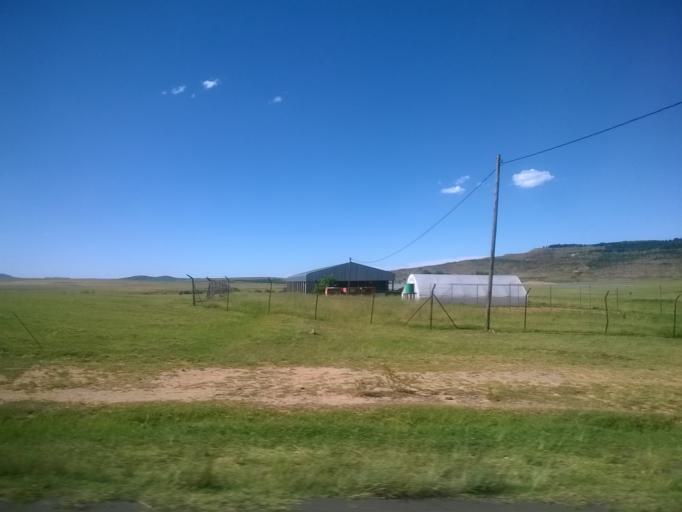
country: LS
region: Maseru
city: Maseru
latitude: -29.2653
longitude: 27.5454
